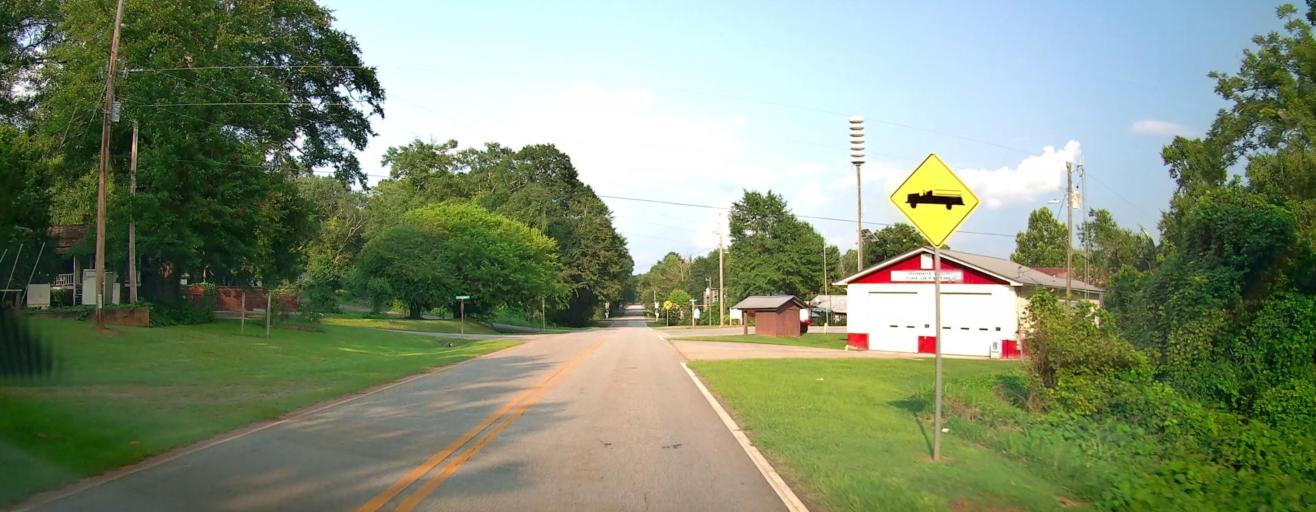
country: US
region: Georgia
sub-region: Monroe County
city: Forsyth
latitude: 33.1070
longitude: -83.8006
